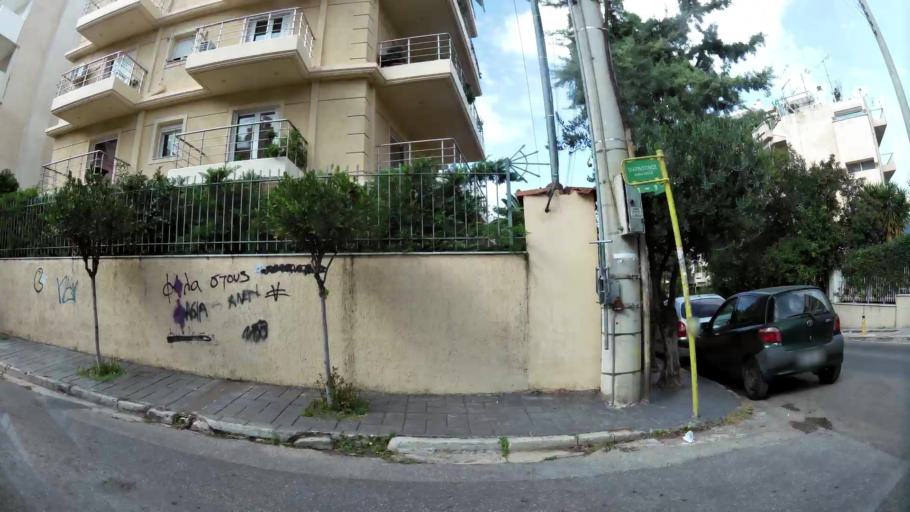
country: GR
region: Attica
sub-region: Nomarchia Athinas
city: Cholargos
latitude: 37.9943
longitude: 23.8009
